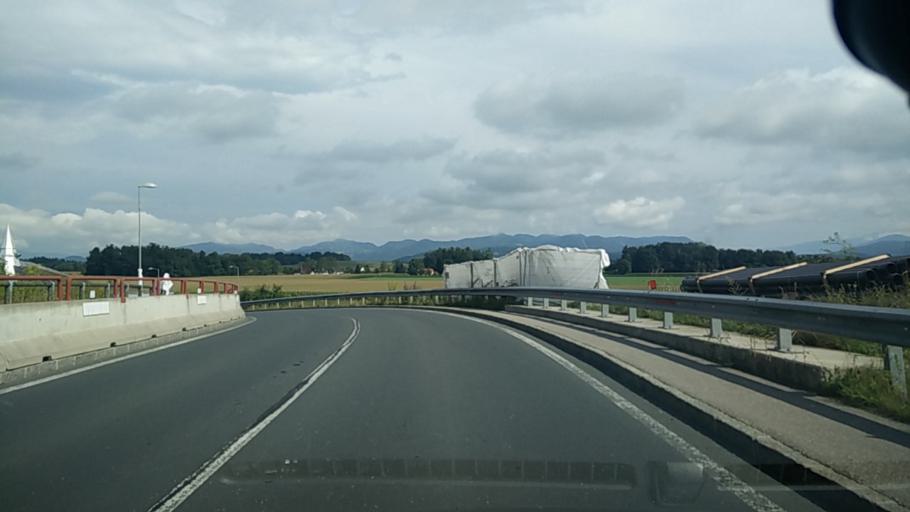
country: AT
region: Carinthia
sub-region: Politischer Bezirk Klagenfurt Land
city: Grafenstein
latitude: 46.6181
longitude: 14.4636
